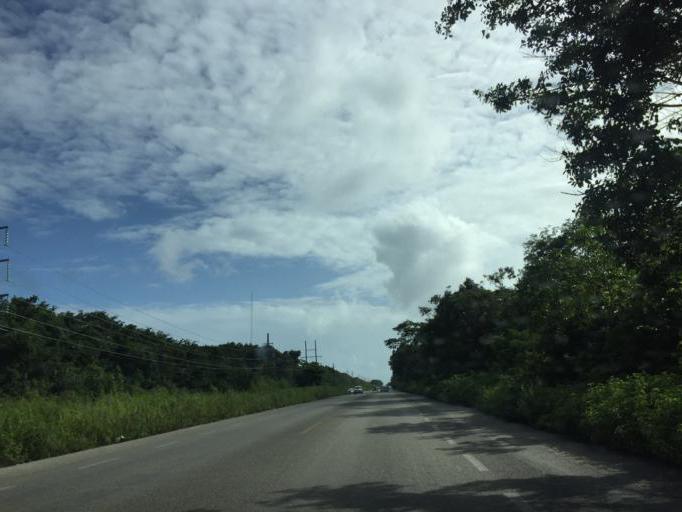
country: MX
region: Quintana Roo
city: Tulum
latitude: 20.2482
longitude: -87.4656
